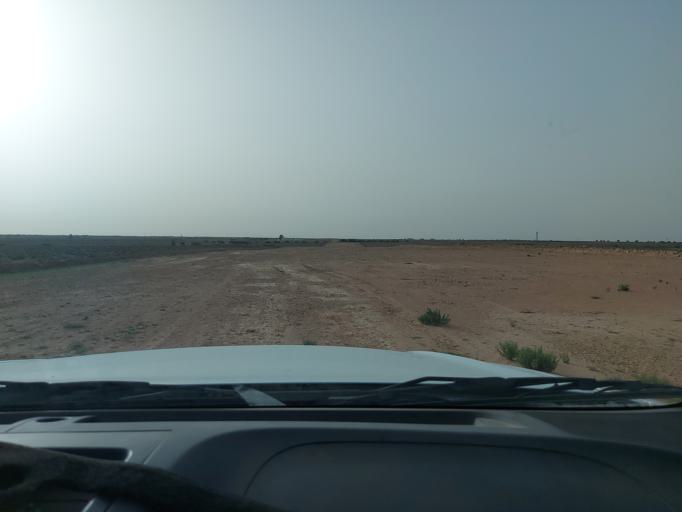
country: TN
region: Madanin
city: Medenine
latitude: 33.3420
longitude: 10.5930
